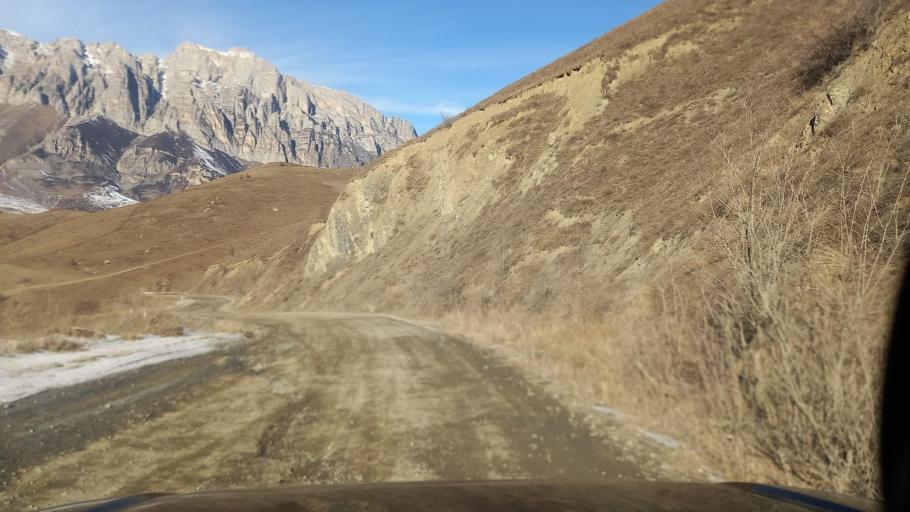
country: RU
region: North Ossetia
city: Verkhniy Fiagdon
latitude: 42.8376
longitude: 44.4669
